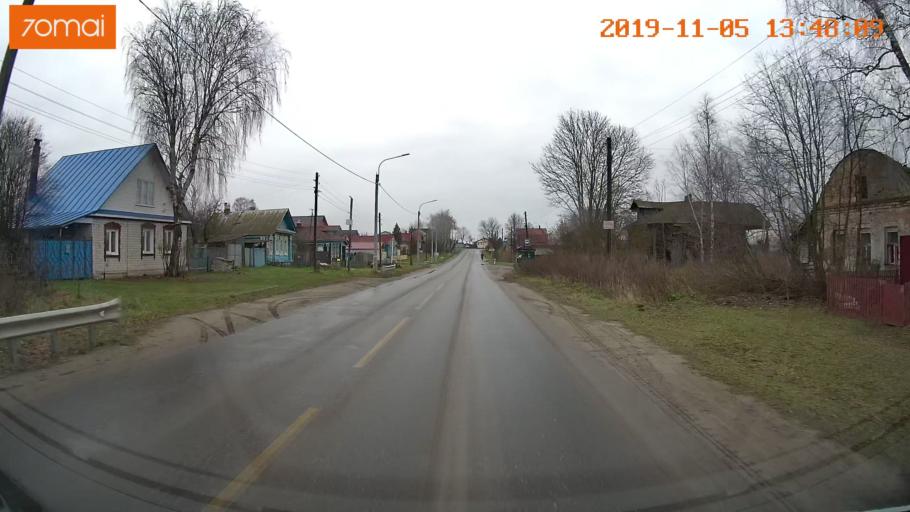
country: RU
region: Ivanovo
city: Shuya
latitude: 57.0020
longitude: 41.4047
